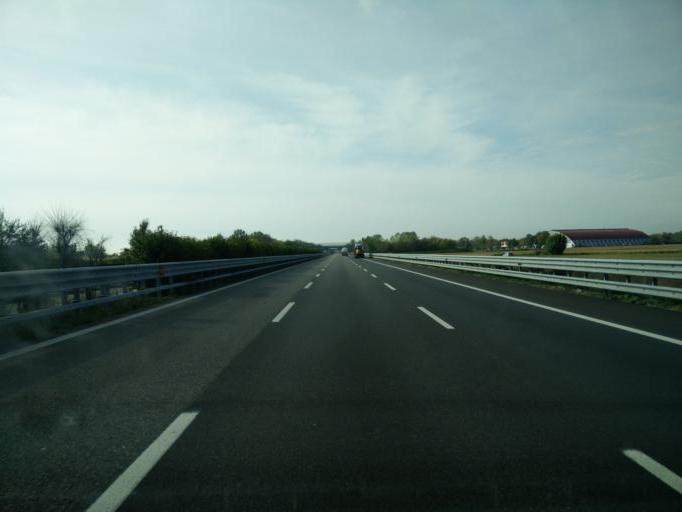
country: IT
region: Lombardy
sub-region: Provincia di Brescia
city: Leno
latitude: 45.3807
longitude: 10.1774
